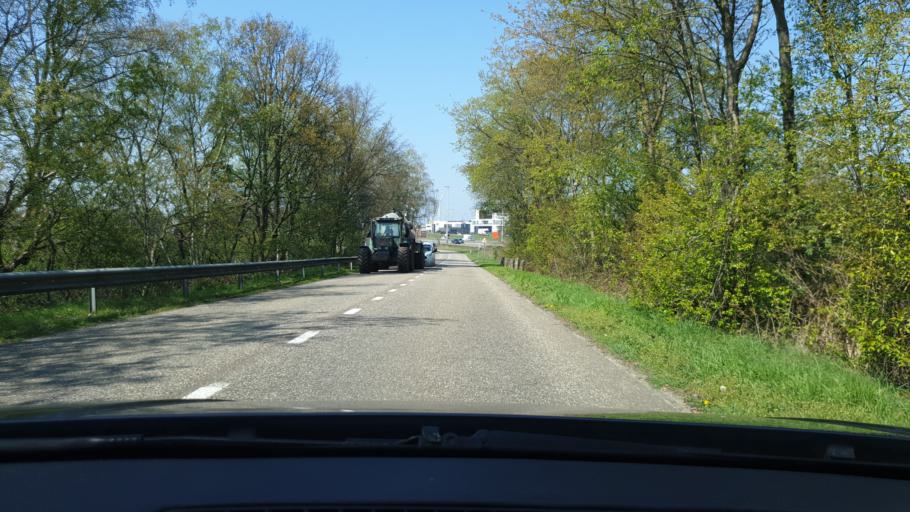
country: BE
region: Flanders
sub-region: Provincie Antwerpen
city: Westerlo
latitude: 51.1236
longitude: 4.9543
